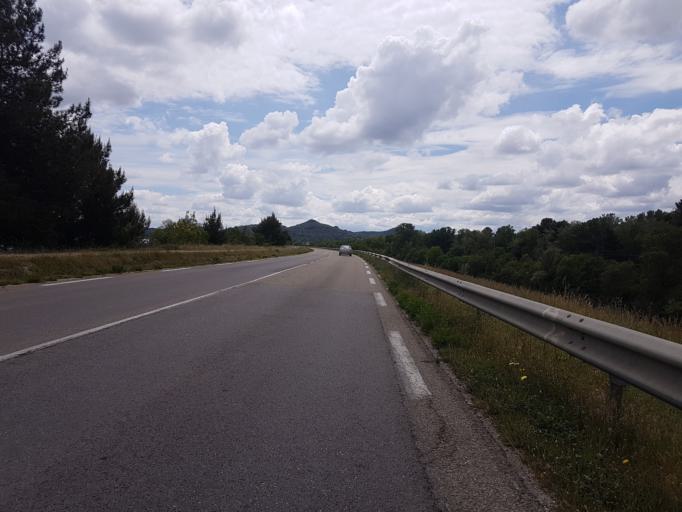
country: FR
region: Languedoc-Roussillon
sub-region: Departement du Gard
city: Vallabregues
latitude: 43.8618
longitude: 4.6188
